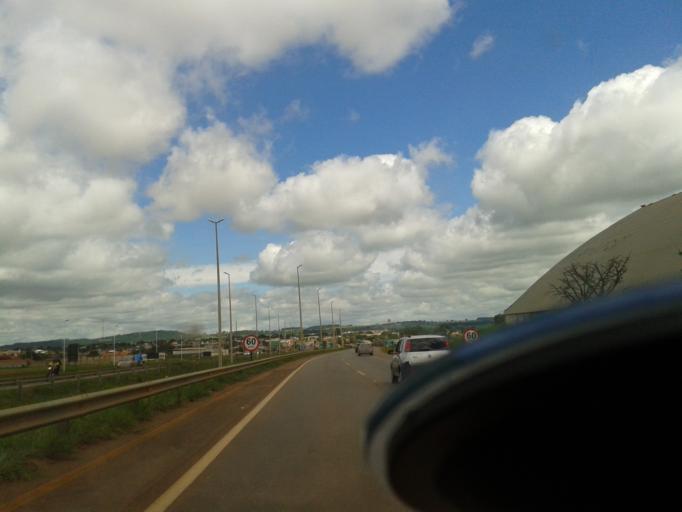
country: BR
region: Goias
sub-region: Goianira
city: Goianira
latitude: -16.5190
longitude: -49.4156
